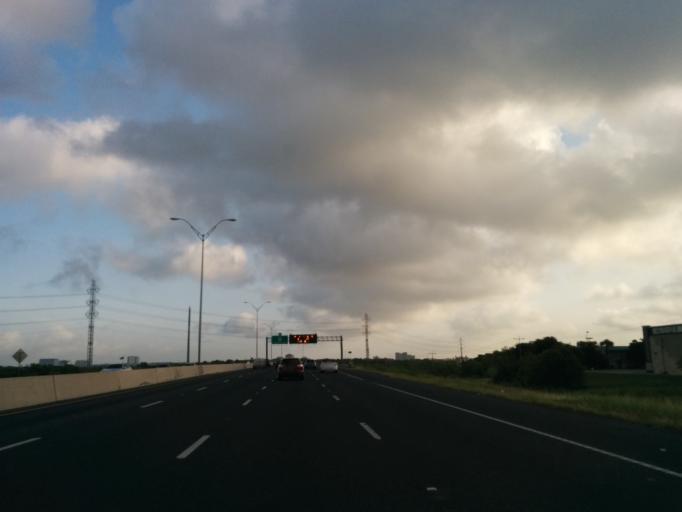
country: US
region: Texas
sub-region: Bexar County
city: Olmos Park
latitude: 29.4922
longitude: -98.4836
